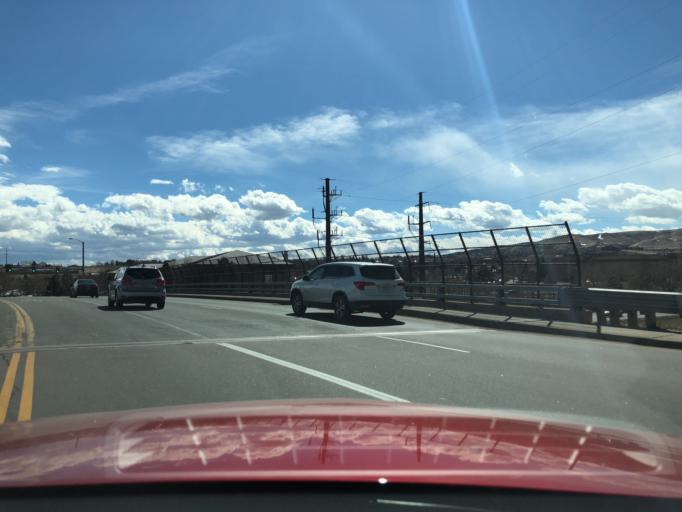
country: US
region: Colorado
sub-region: Jefferson County
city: Applewood
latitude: 39.7404
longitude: -105.1598
